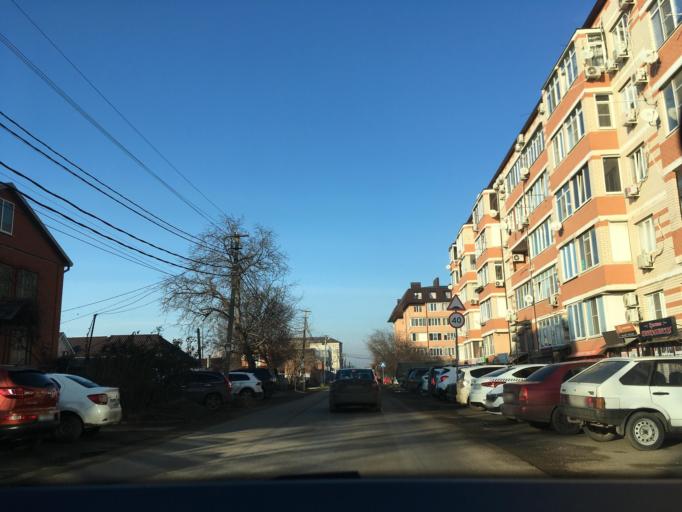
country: RU
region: Krasnodarskiy
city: Krasnodar
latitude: 45.0734
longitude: 39.0212
